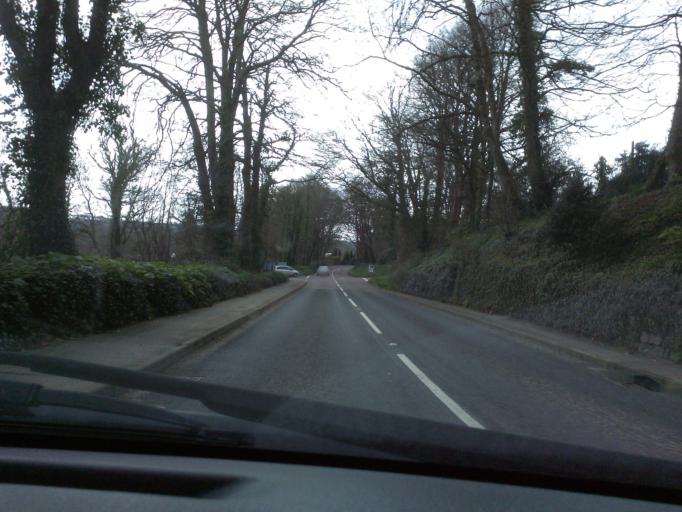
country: GB
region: England
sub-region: Cornwall
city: Penzance
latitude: 50.1104
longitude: -5.5629
